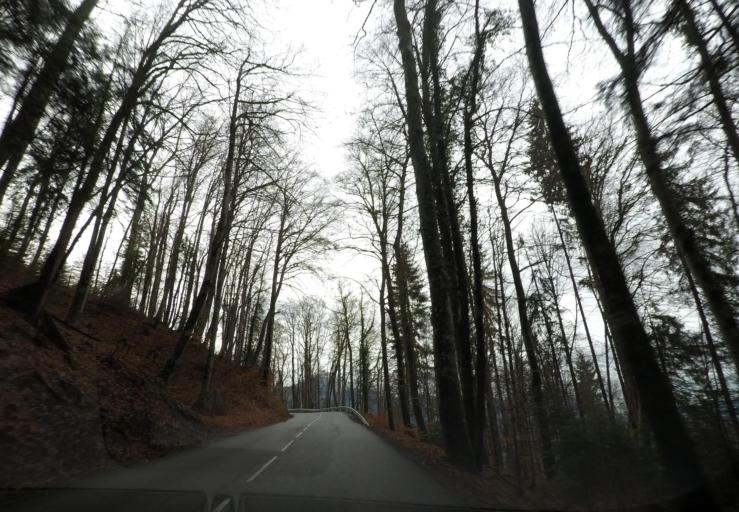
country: FR
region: Rhone-Alpes
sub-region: Departement de la Haute-Savoie
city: Chatillon-sur-Cluses
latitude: 46.0799
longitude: 6.5941
